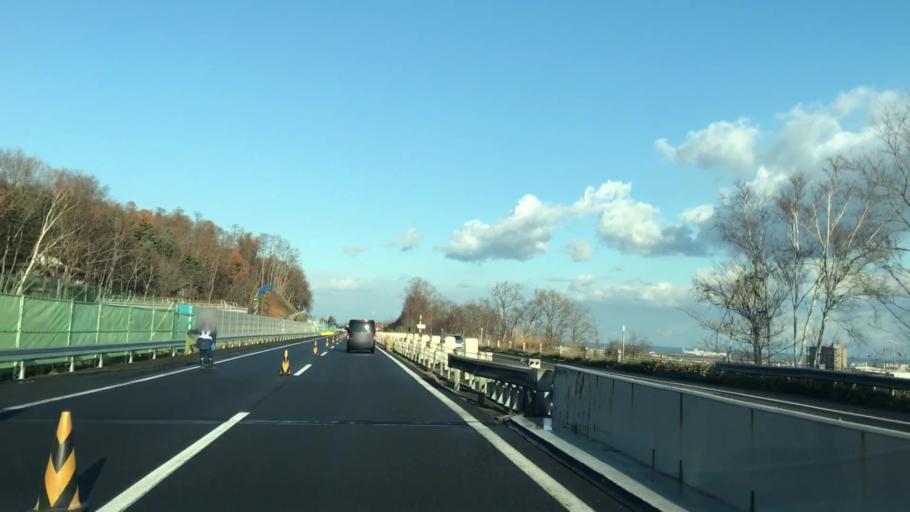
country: JP
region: Hokkaido
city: Sapporo
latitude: 43.1109
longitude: 141.2395
